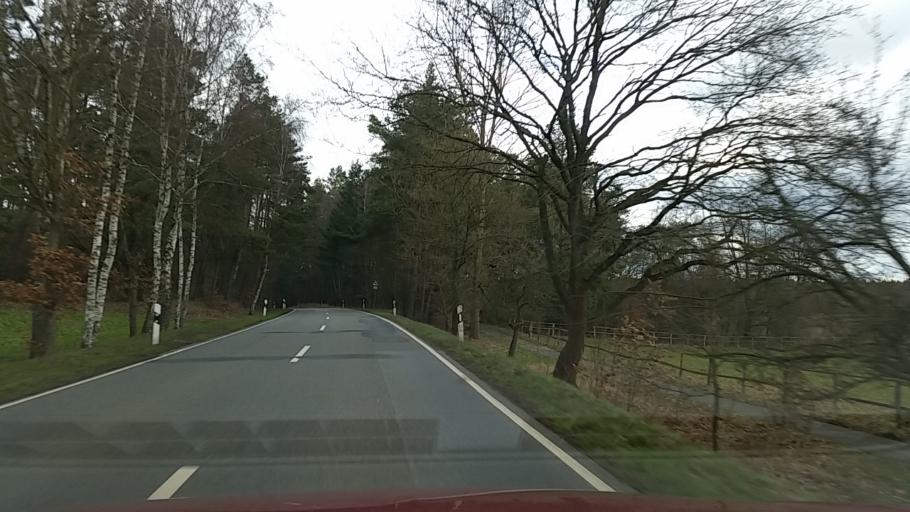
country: DE
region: Lower Saxony
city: Zernien
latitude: 53.0988
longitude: 10.9458
